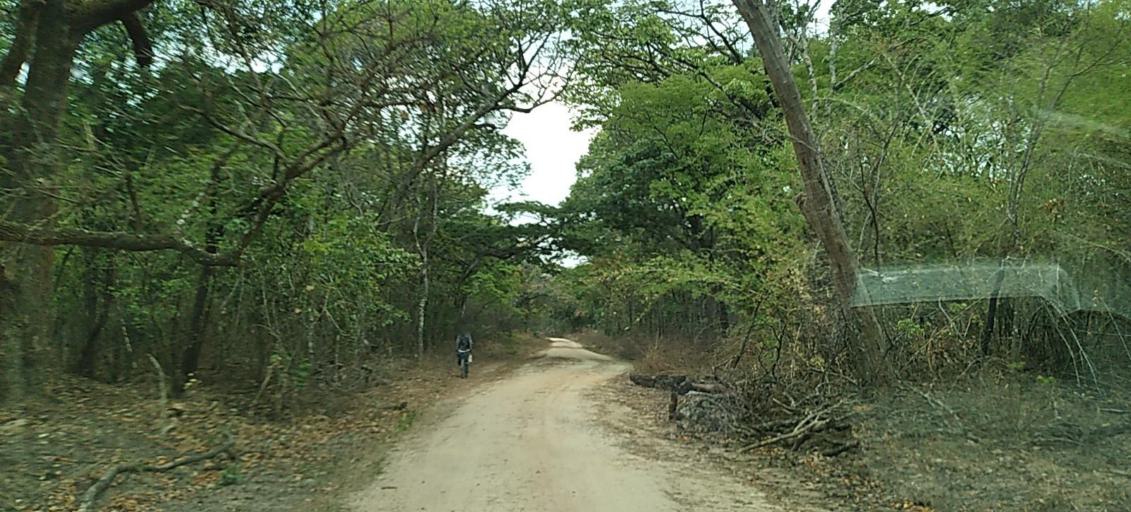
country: ZM
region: Copperbelt
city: Chingola
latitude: -12.7545
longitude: 27.7122
